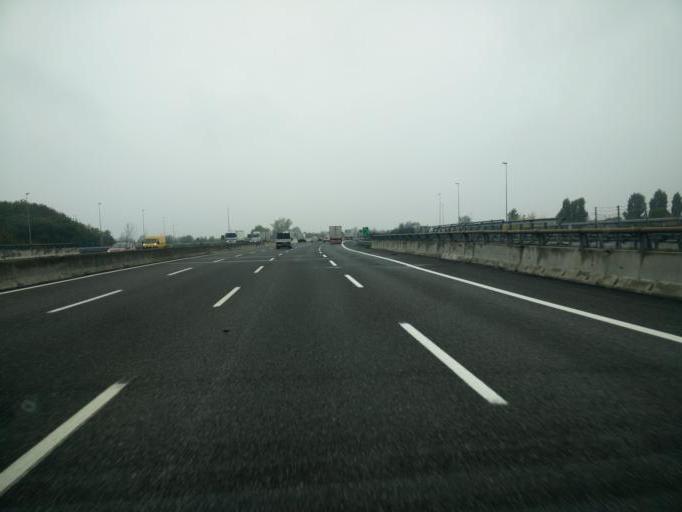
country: IT
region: Emilia-Romagna
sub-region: Provincia di Modena
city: Baggiovara
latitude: 44.6165
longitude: 10.8896
